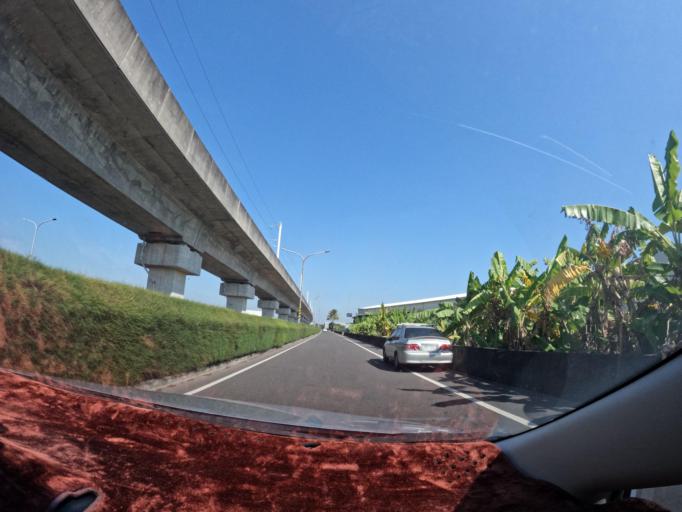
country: TW
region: Taiwan
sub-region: Tainan
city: Tainan
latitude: 23.0086
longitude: 120.2866
